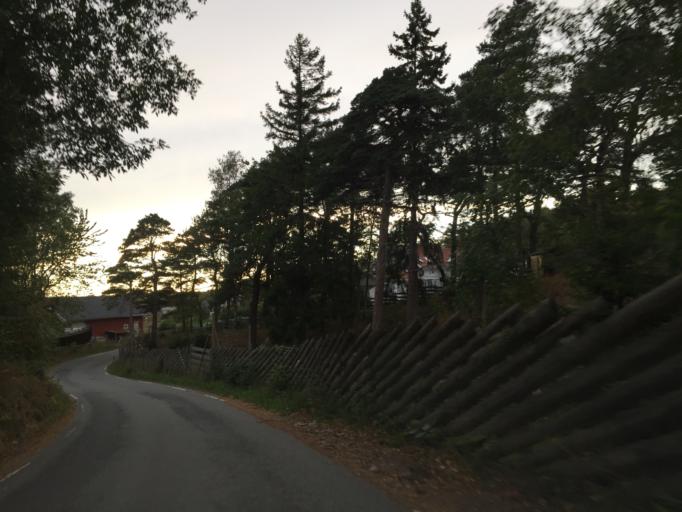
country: NO
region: Ostfold
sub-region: Hvaler
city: Skjaerhalden
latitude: 59.0590
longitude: 11.0073
